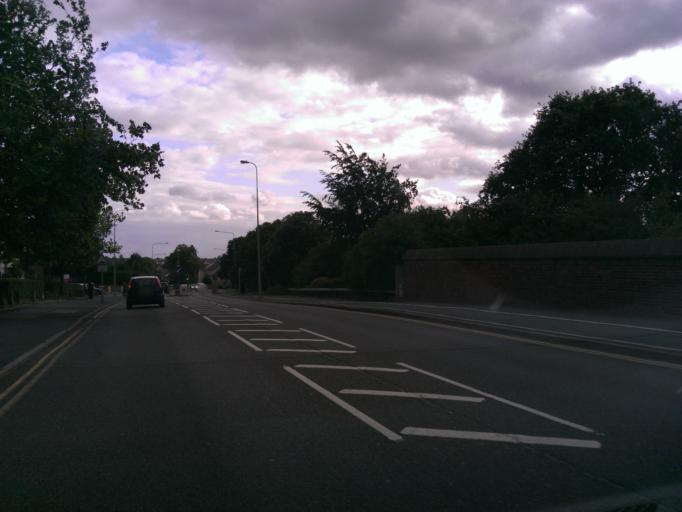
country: GB
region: England
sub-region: Essex
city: Colchester
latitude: 51.8994
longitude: 0.9210
